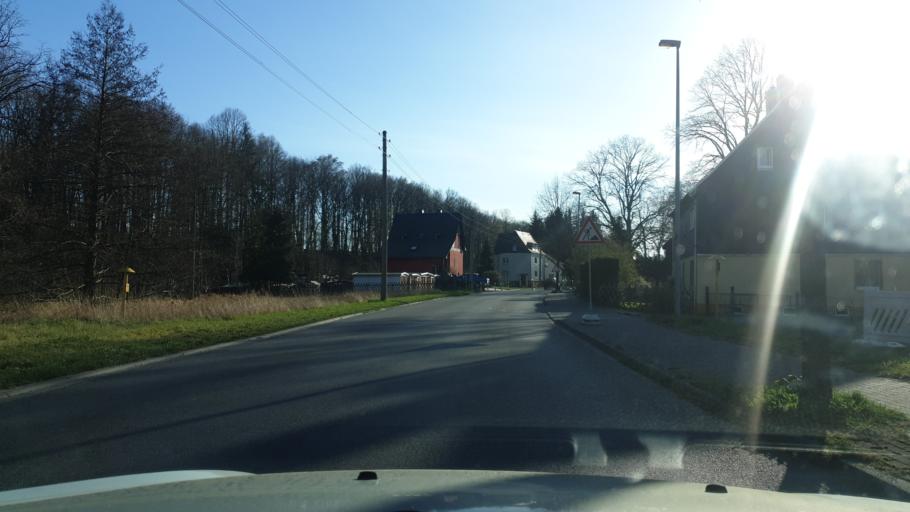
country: DE
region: Saxony
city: Neukirchen
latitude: 50.7714
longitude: 12.9017
